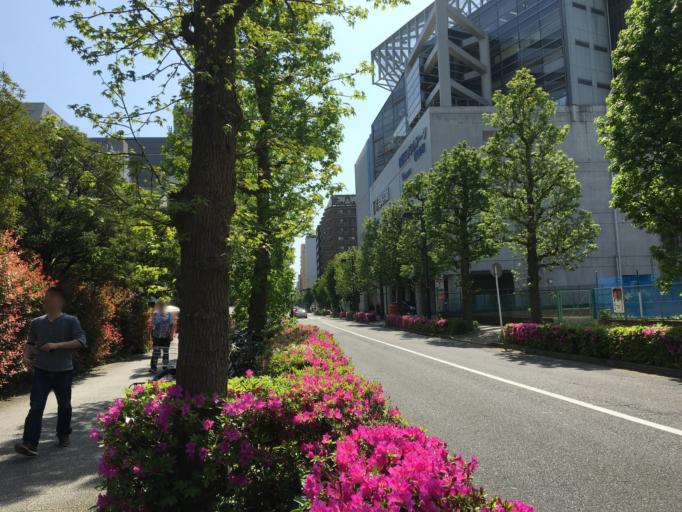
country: JP
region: Kanagawa
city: Yokohama
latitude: 35.5127
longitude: 139.6192
